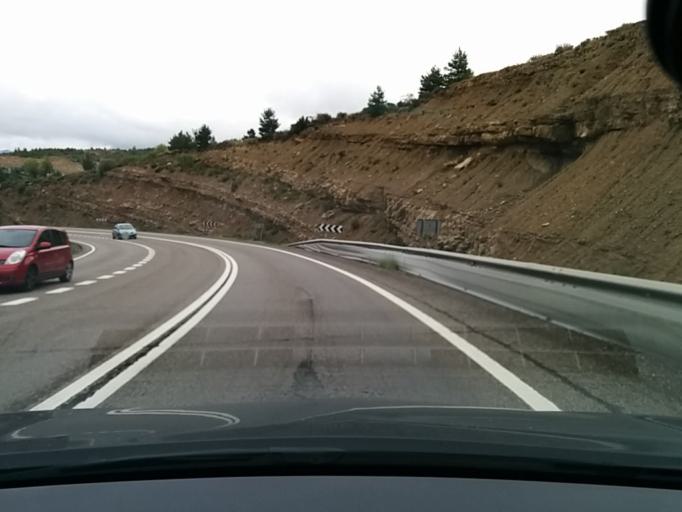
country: ES
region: Aragon
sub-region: Provincia de Huesca
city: Arguis
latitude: 42.4018
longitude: -0.3831
